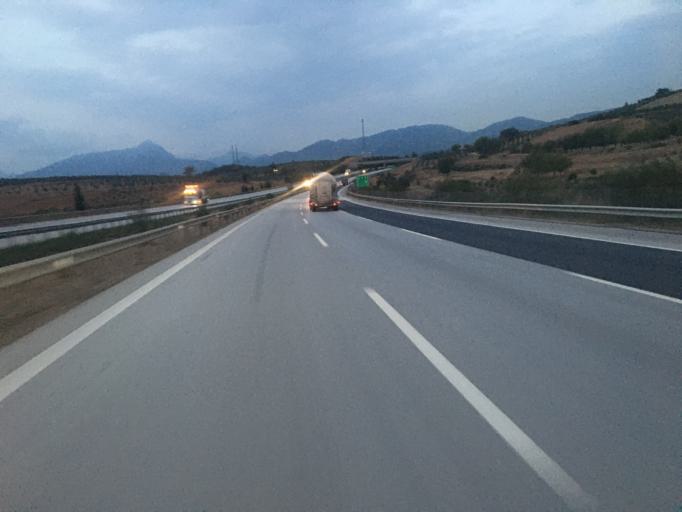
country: TR
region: Osmaniye
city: Haruniye
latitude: 37.1972
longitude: 36.3838
